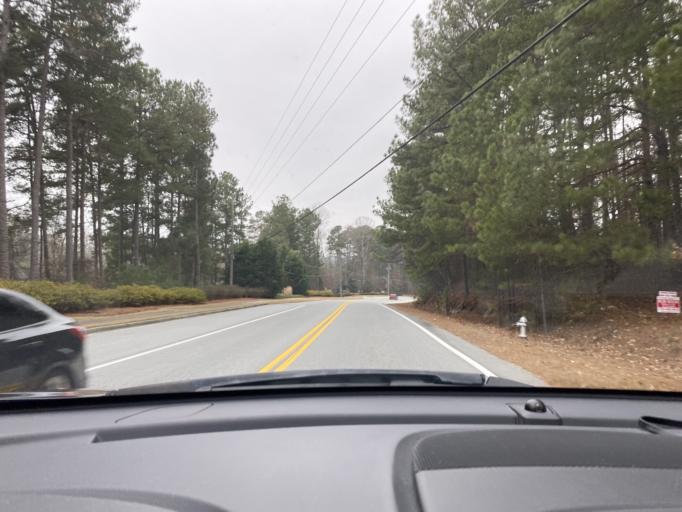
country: US
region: Georgia
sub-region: Gwinnett County
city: Dacula
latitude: 33.9156
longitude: -83.8660
